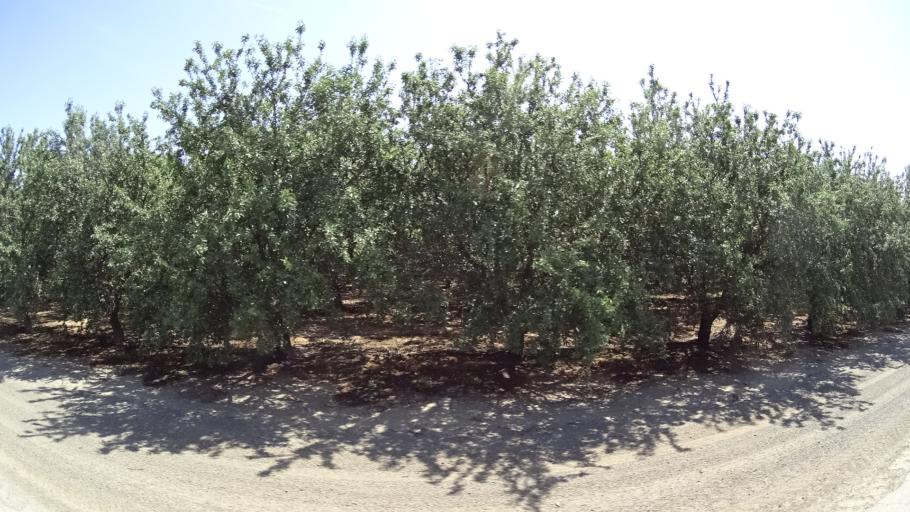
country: US
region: California
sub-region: Kings County
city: Kettleman City
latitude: 36.0968
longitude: -120.0037
